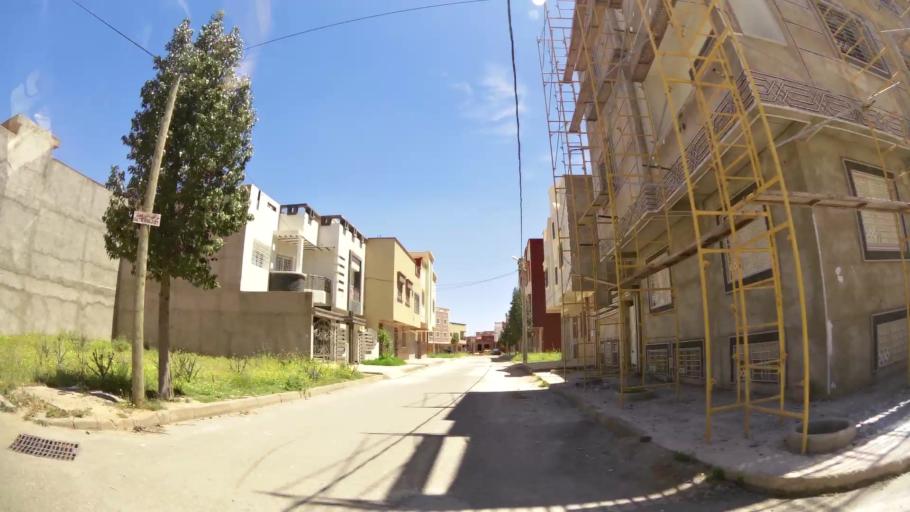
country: MA
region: Oriental
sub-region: Oujda-Angad
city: Oujda
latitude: 34.6641
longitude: -1.9400
